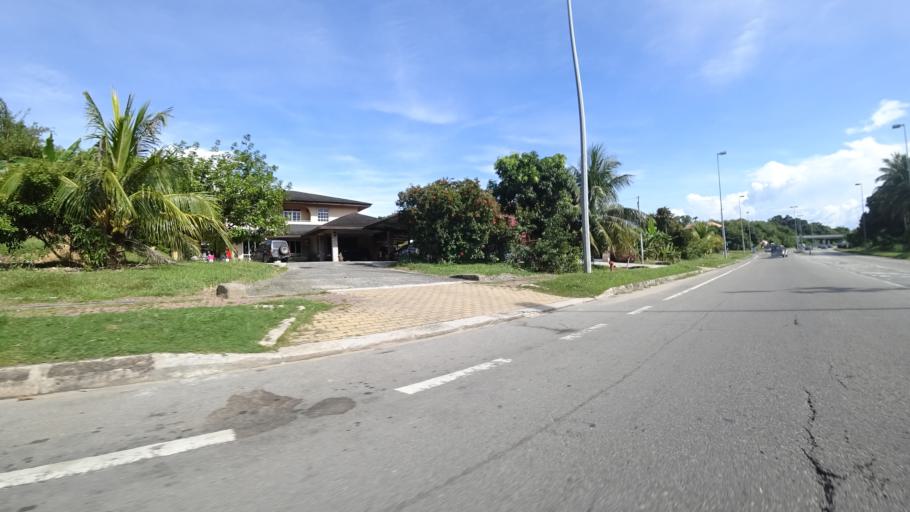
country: BN
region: Brunei and Muara
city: Bandar Seri Begawan
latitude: 4.9538
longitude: 114.8411
